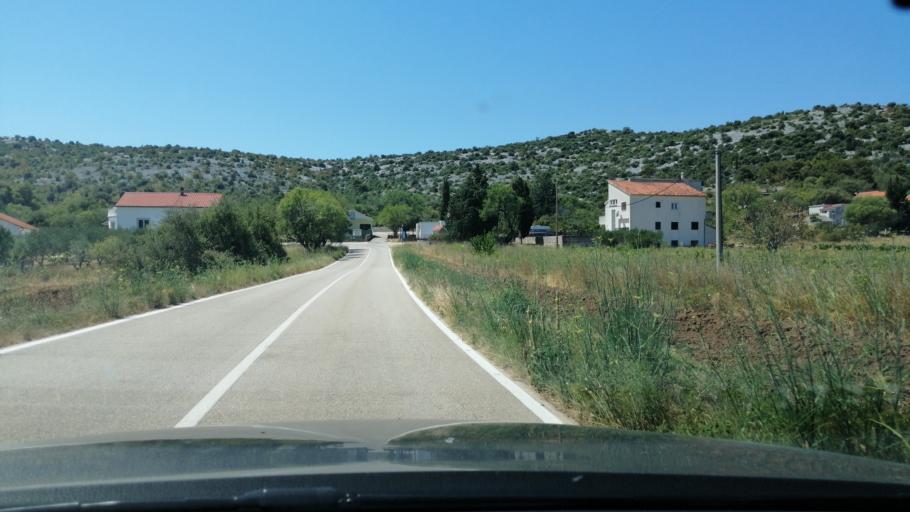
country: HR
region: Sibensko-Kniniska
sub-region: Grad Sibenik
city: Pirovac
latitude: 43.8718
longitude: 15.6801
